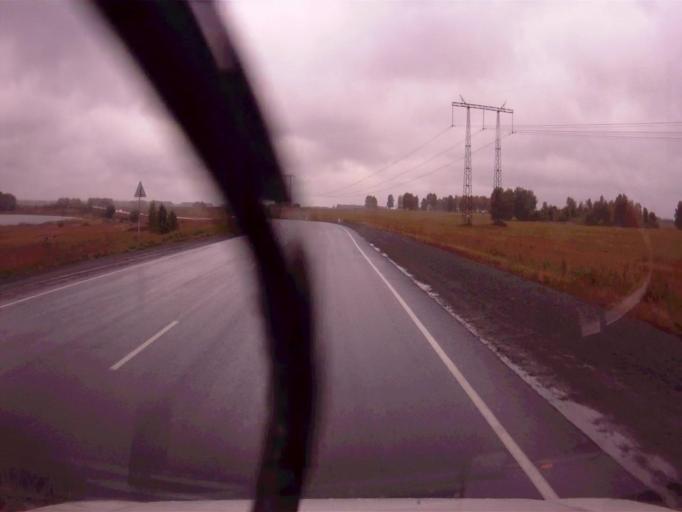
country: RU
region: Chelyabinsk
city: Roshchino
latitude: 55.3907
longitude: 61.1230
